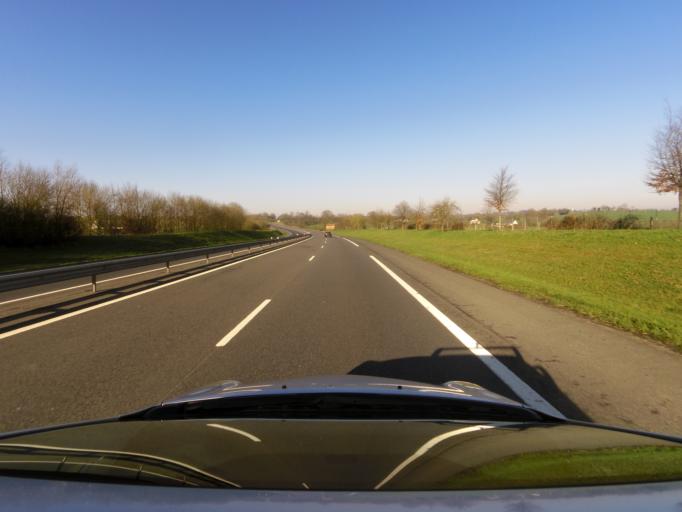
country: FR
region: Lower Normandy
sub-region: Departement du Calvados
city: Saint-Martin-des-Besaces
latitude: 49.0149
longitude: -0.8710
